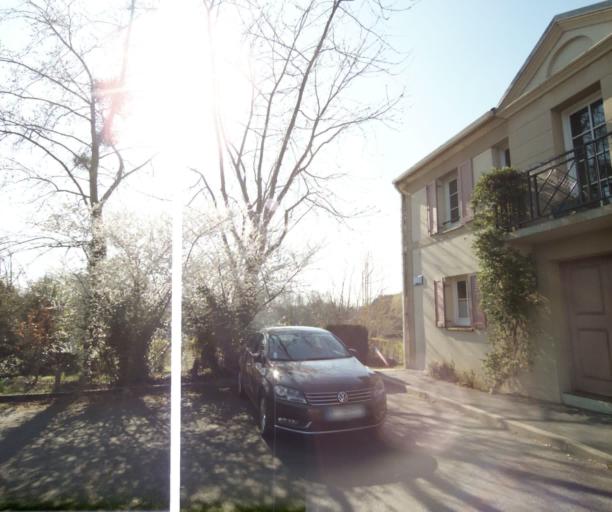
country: FR
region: Ile-de-France
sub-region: Departement du Val-d'Oise
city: Neuville-sur-Oise
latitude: 49.0284
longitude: 2.0628
